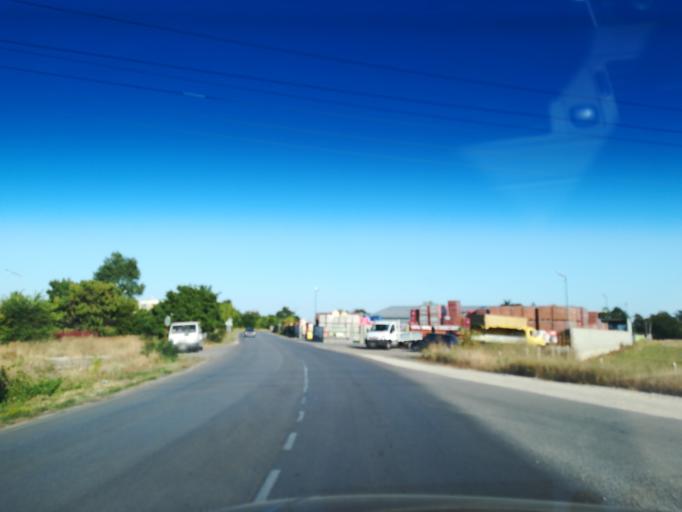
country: BG
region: Stara Zagora
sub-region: Obshtina Chirpan
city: Chirpan
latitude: 42.0936
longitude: 25.2112
